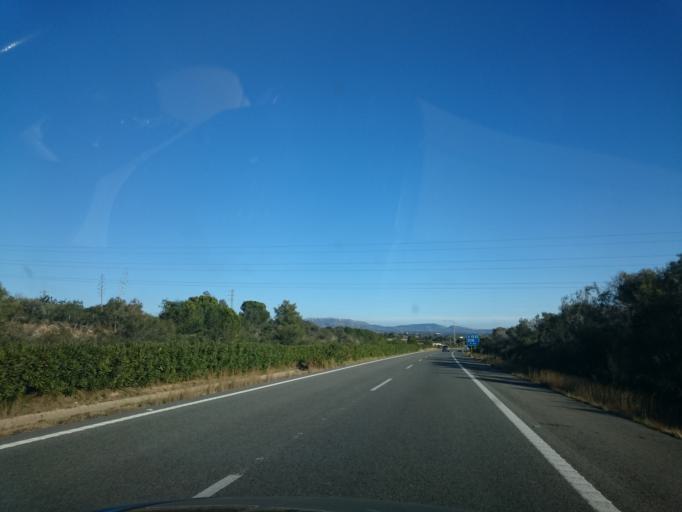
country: ES
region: Catalonia
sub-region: Provincia de Tarragona
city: Masdenverge
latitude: 40.7104
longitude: 0.5540
